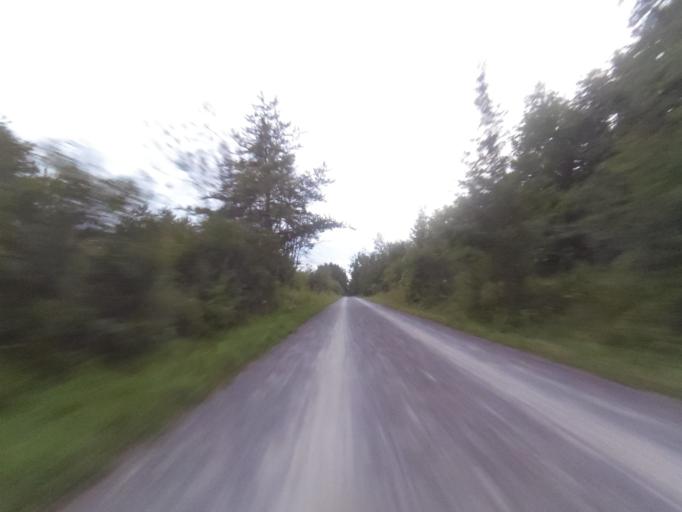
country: CA
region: Ontario
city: Bells Corners
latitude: 45.3059
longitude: -75.8565
